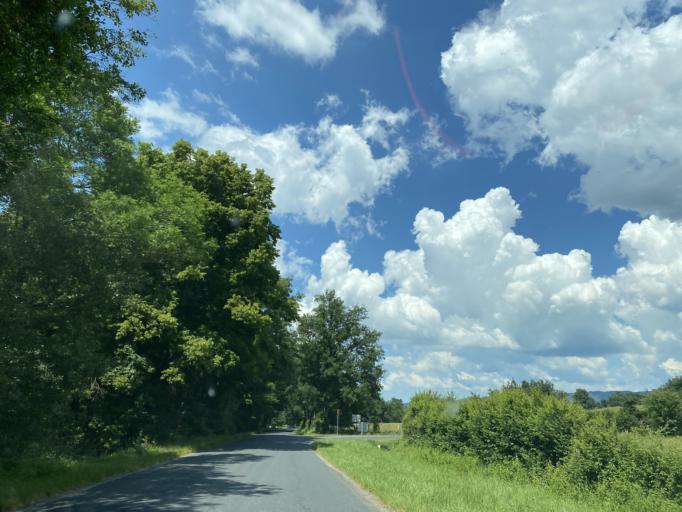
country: FR
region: Auvergne
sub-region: Departement du Puy-de-Dome
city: Courpiere
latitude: 45.7721
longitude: 3.5501
